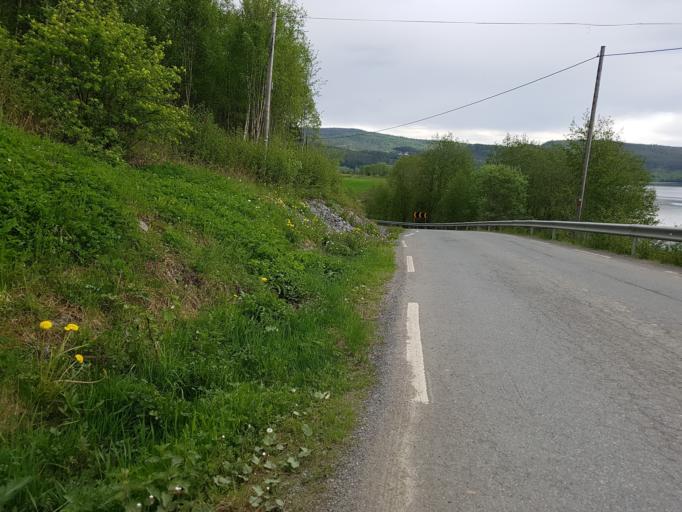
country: NO
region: Nord-Trondelag
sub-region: Levanger
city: Skogn
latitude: 63.6262
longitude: 11.2742
